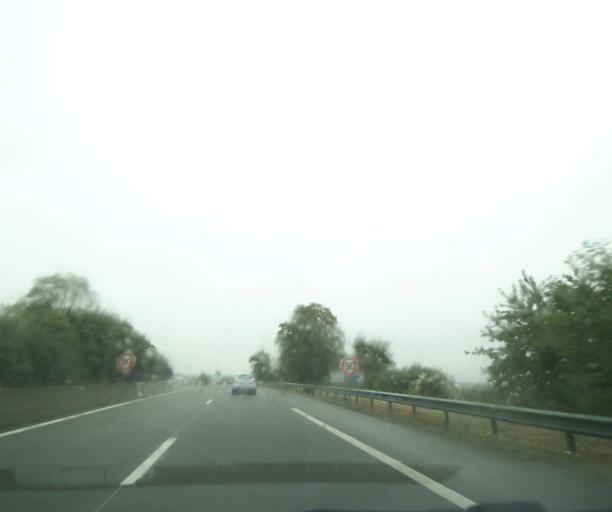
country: FR
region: Auvergne
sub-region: Departement du Puy-de-Dome
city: Menetrol
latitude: 45.8675
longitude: 3.1189
